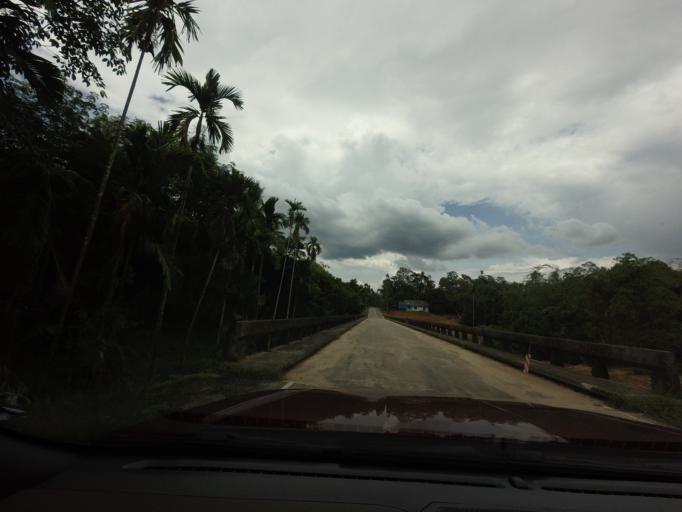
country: TH
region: Narathiwat
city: Sukhirin
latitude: 5.9983
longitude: 101.6990
